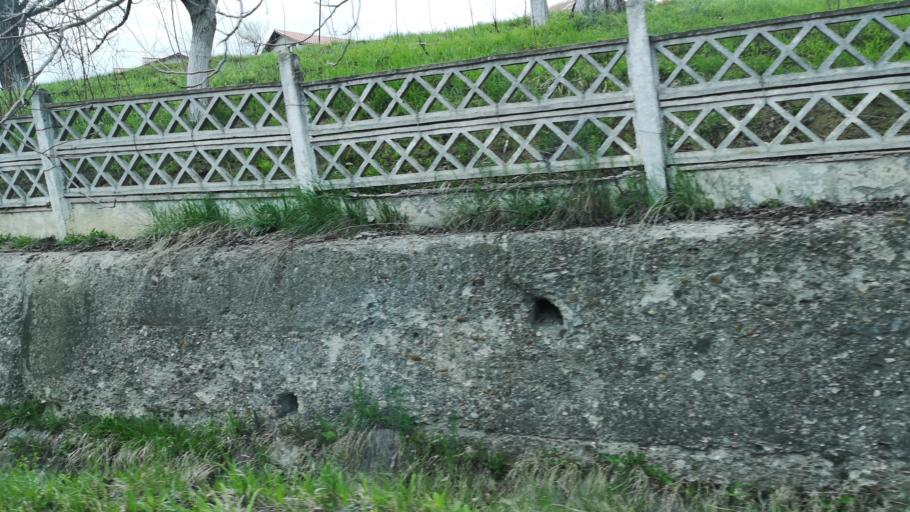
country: RO
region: Prahova
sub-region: Comuna Soimari
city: Soimari
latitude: 45.1566
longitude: 26.2040
